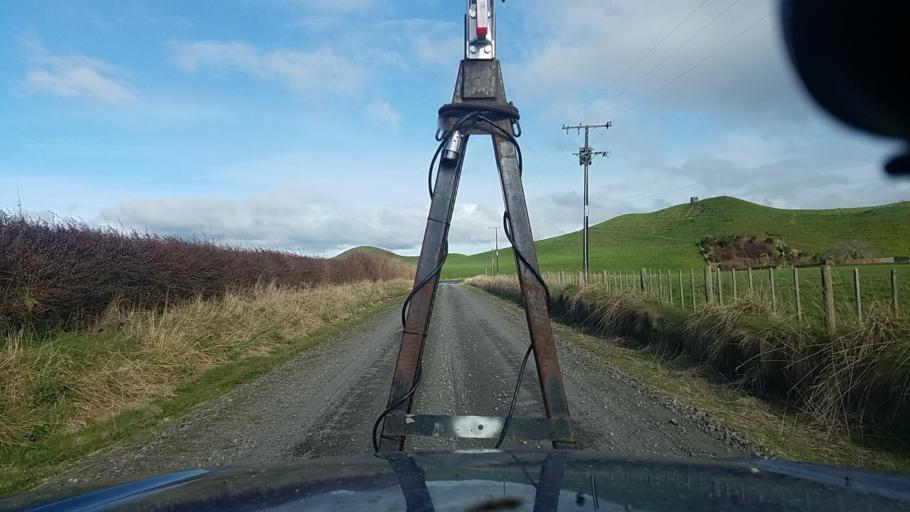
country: NZ
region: Taranaki
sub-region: South Taranaki District
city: Eltham
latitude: -39.3448
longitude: 174.4211
